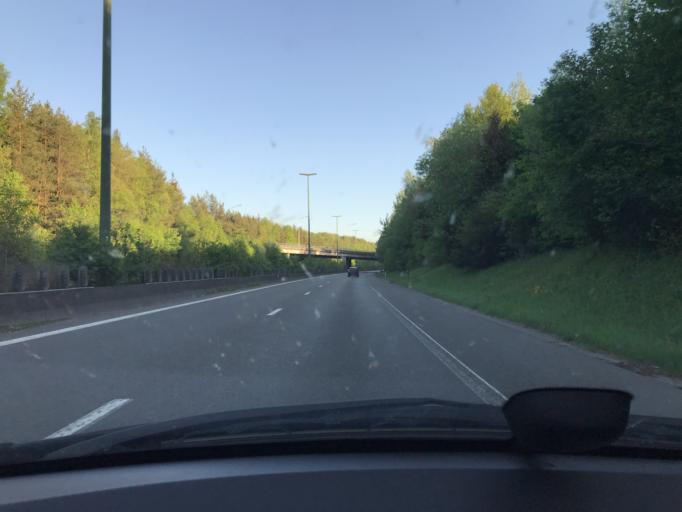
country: BE
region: Wallonia
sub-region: Province du Luxembourg
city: Tellin
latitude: 50.0534
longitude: 5.2089
